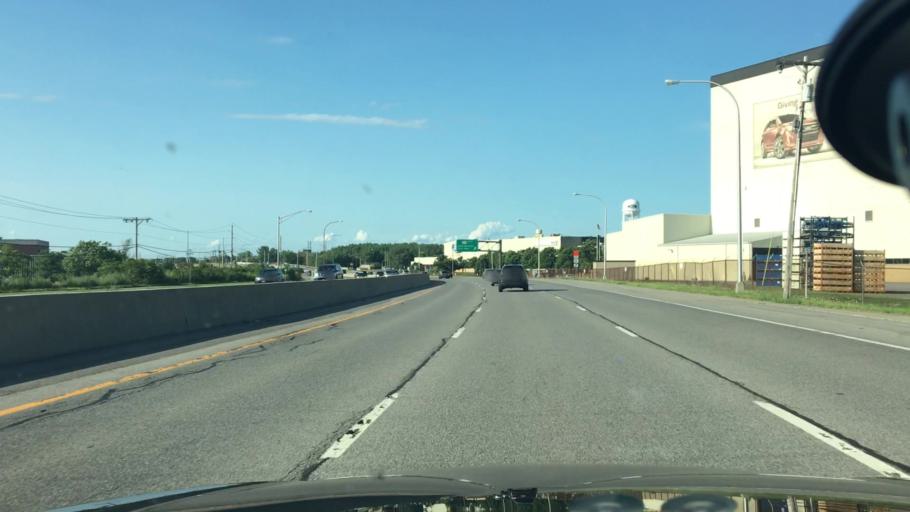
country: US
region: New York
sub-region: Erie County
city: Blasdell
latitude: 42.7845
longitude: -78.8484
